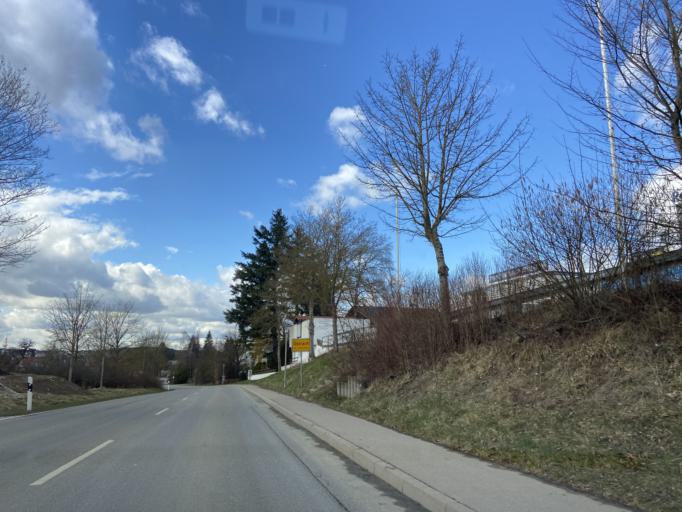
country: DE
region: Baden-Wuerttemberg
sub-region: Tuebingen Region
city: Ostrach
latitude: 47.9509
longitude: 9.3912
